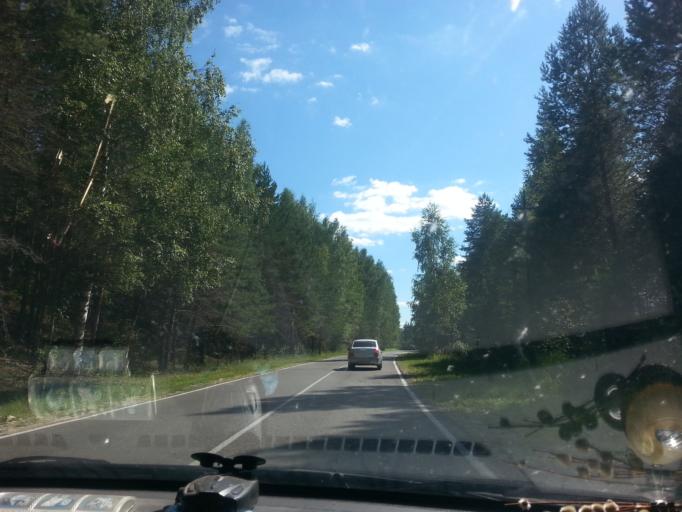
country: RU
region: Vladimir
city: Galitsy
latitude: 56.0072
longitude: 42.8605
